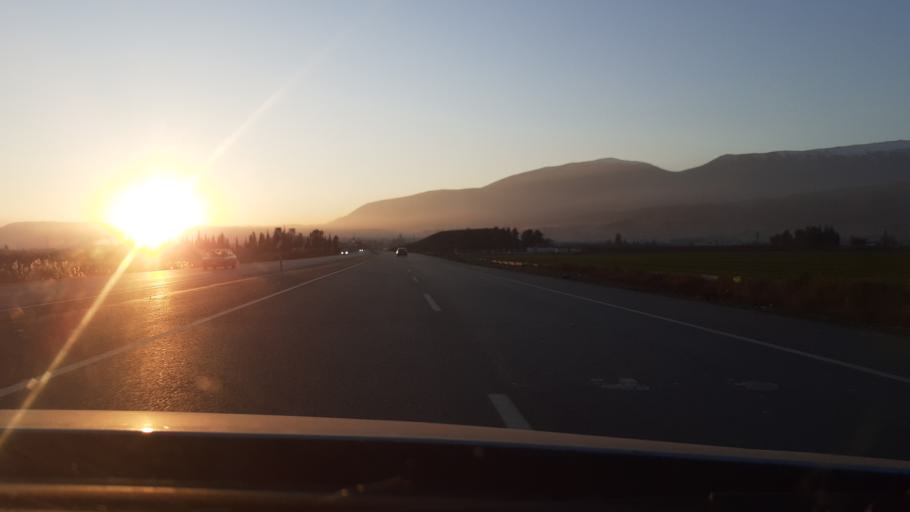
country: TR
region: Hatay
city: Kirikhan
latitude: 36.5035
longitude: 36.4005
